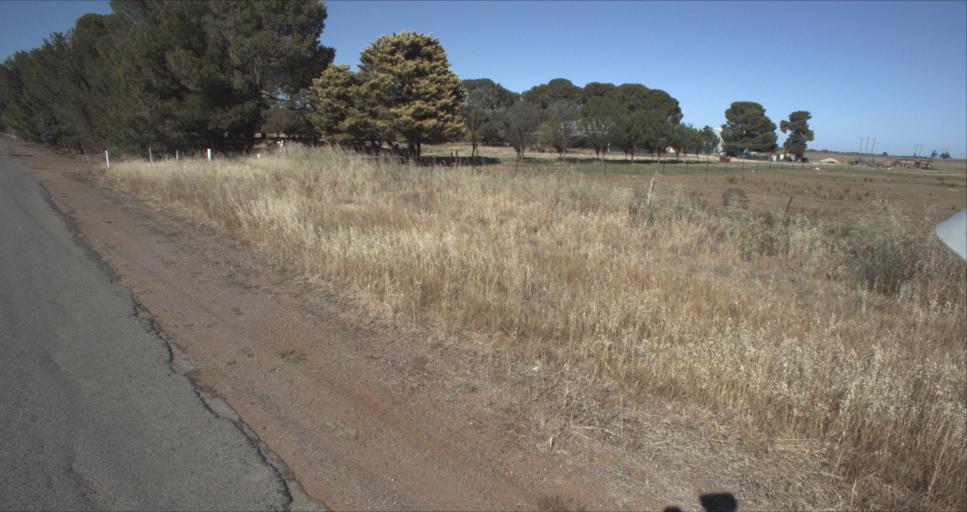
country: AU
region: New South Wales
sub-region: Leeton
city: Leeton
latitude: -34.5715
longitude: 146.3105
